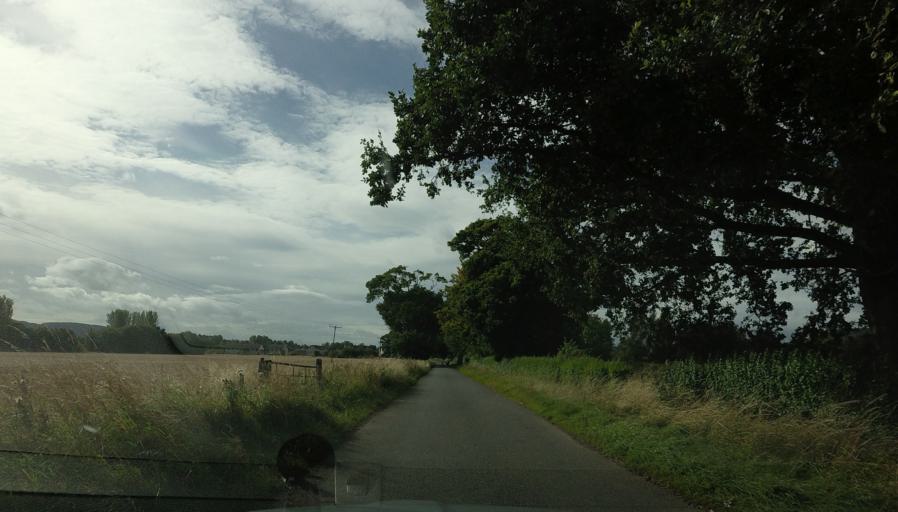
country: GB
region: Scotland
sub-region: Perth and Kinross
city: Bridge of Earn
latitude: 56.3455
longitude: -3.3869
